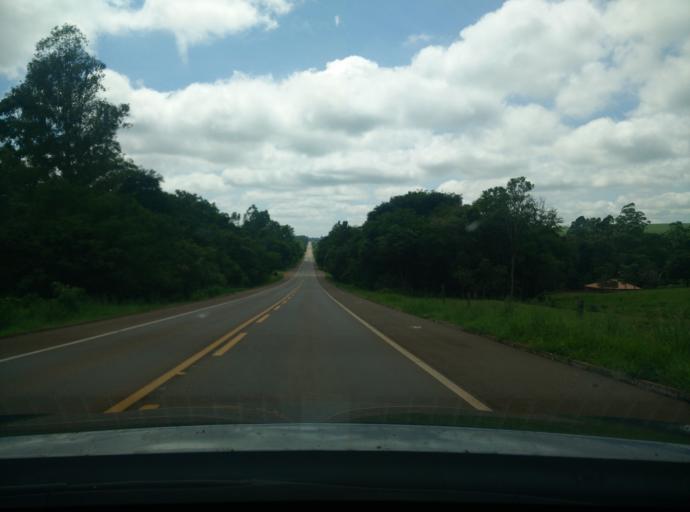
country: BR
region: Parana
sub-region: Campo Mourao
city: Campo Mourao
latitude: -23.9792
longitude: -52.5399
